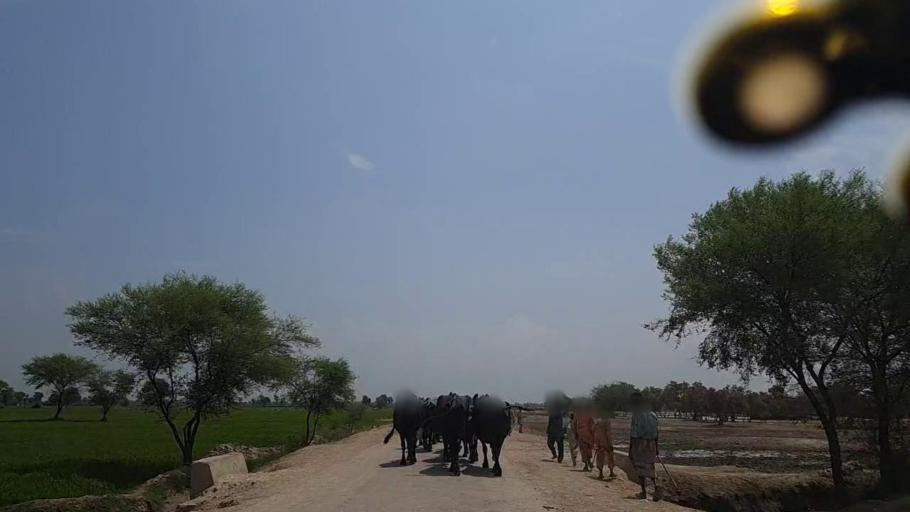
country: PK
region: Sindh
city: Thul
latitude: 28.1153
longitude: 68.8574
